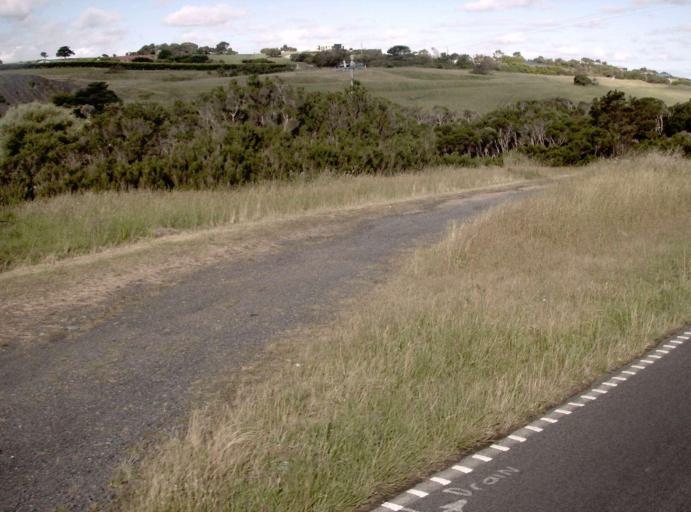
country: AU
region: Victoria
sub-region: Bass Coast
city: North Wonthaggi
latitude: -38.5444
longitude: 145.4614
